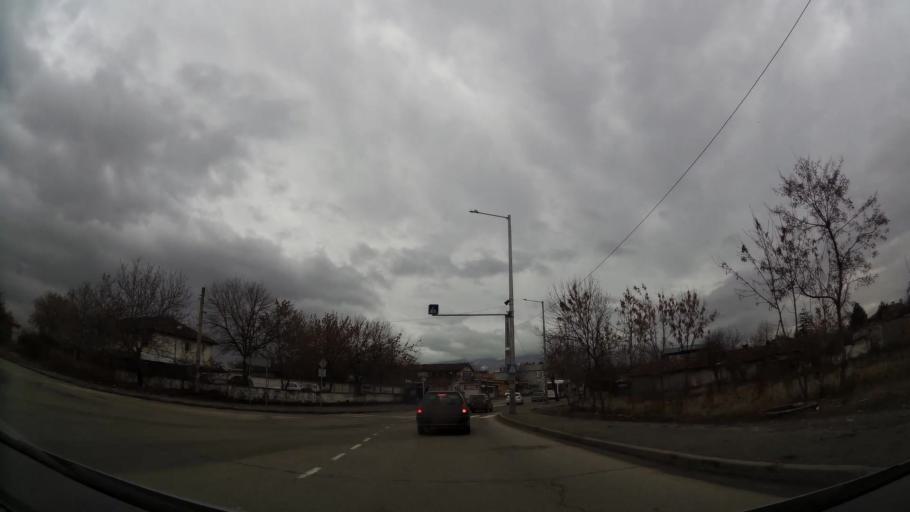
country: BG
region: Sofia-Capital
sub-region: Stolichna Obshtina
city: Sofia
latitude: 42.7254
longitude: 23.2815
